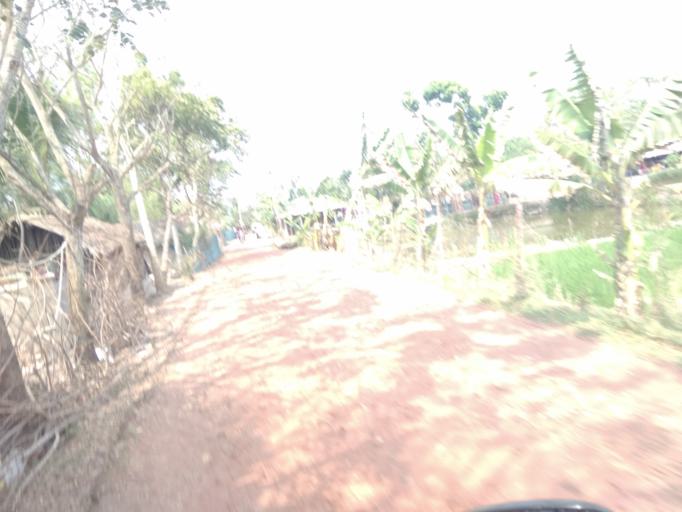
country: IN
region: West Bengal
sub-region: North 24 Parganas
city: Taki
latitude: 22.3018
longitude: 89.2681
